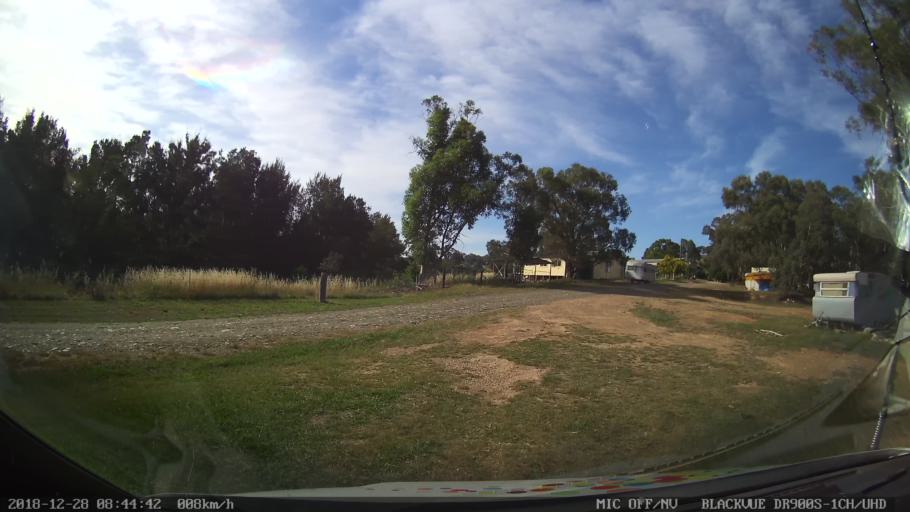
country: AU
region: New South Wales
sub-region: Upper Lachlan Shire
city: Crookwell
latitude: -34.0153
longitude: 149.3282
